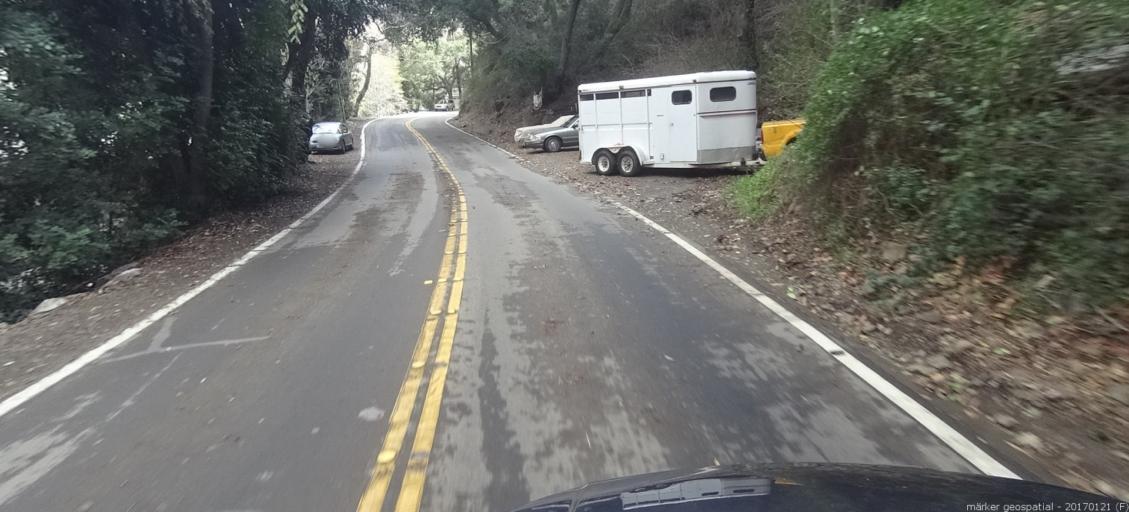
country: US
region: California
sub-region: Orange County
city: Portola Hills
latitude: 33.7473
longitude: -117.6132
